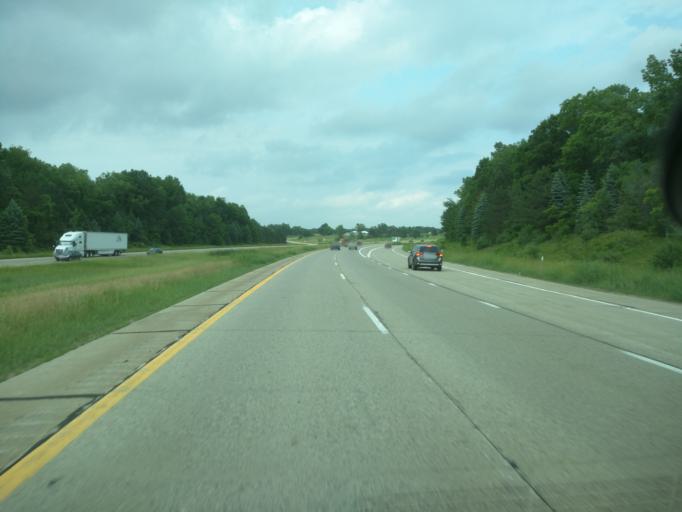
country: US
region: Michigan
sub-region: Clinton County
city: DeWitt
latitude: 42.8136
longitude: -84.5806
